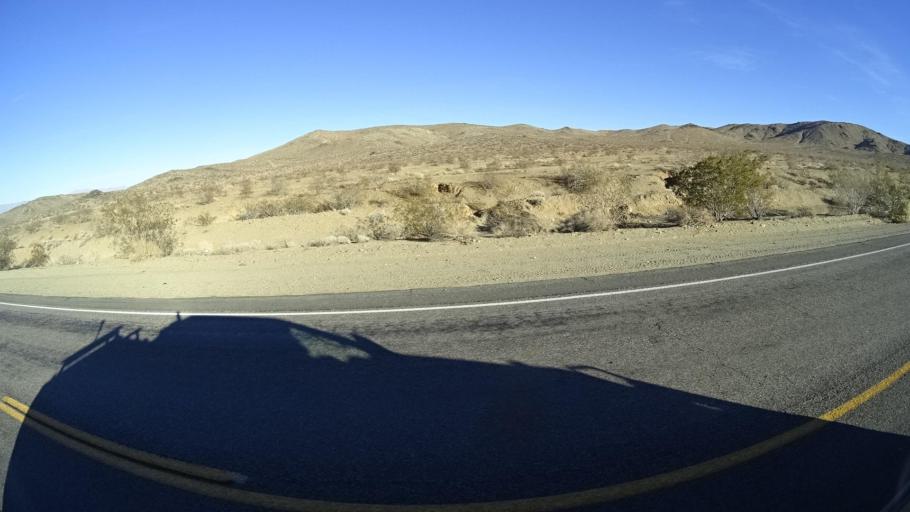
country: US
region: California
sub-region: Kern County
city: Ridgecrest
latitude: 35.5688
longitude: -117.7140
